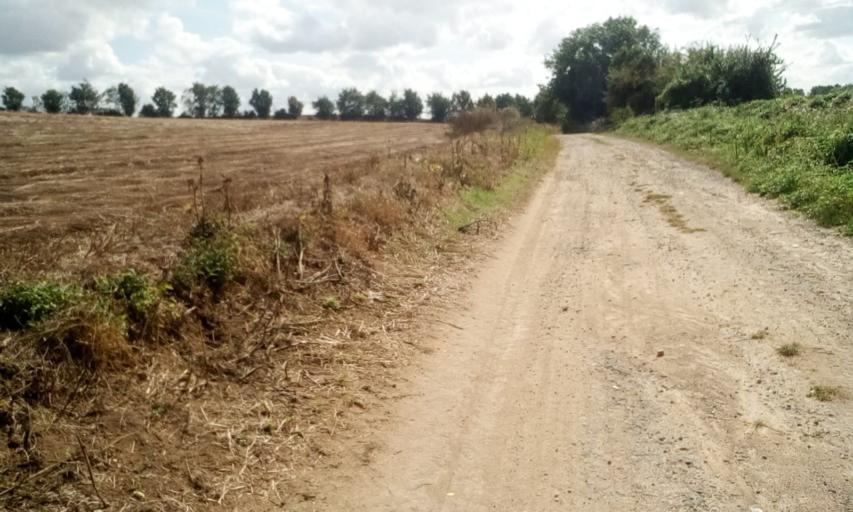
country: FR
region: Lower Normandy
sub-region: Departement du Calvados
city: Moult
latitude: 49.0988
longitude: -0.1891
